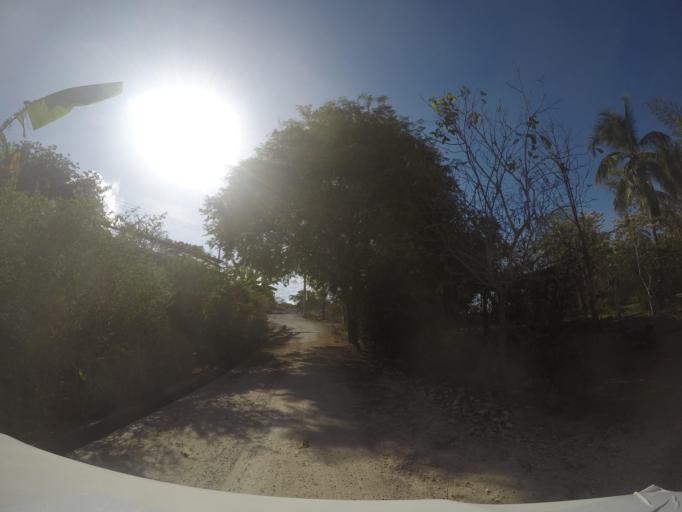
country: TL
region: Baucau
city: Baucau
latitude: -8.4550
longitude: 126.4424
